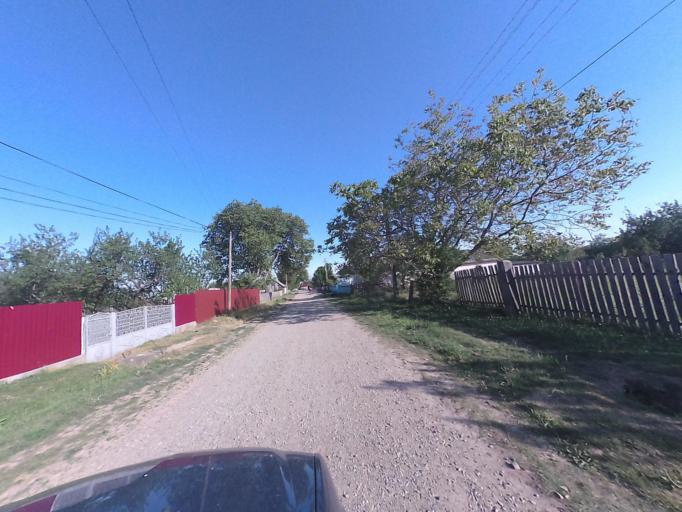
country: RO
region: Neamt
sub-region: Comuna Cordun
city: Pildesti
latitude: 46.9823
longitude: 26.8080
